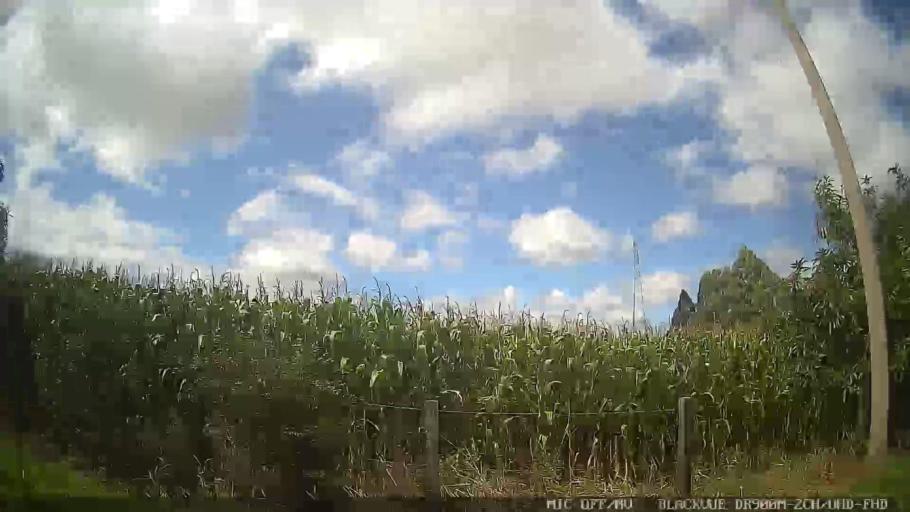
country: BR
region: Sao Paulo
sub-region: Amparo
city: Amparo
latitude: -22.8640
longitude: -46.7244
